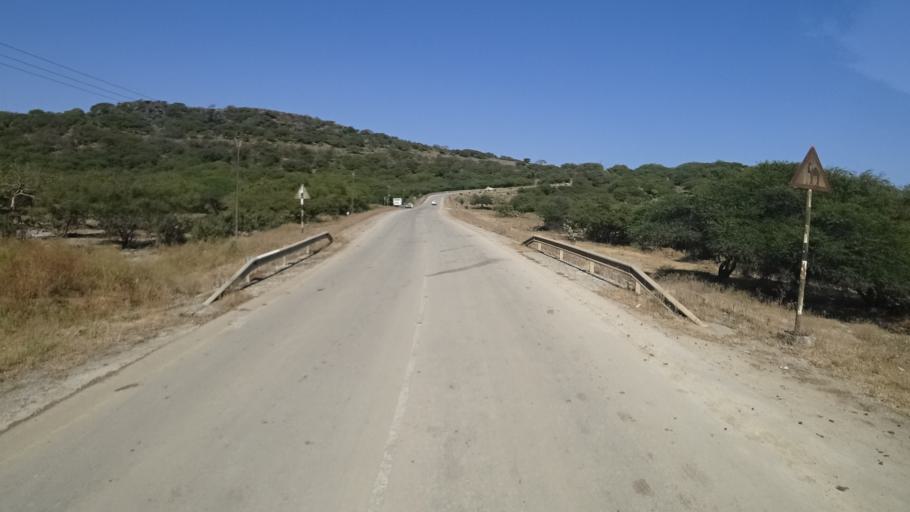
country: OM
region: Zufar
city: Salalah
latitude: 17.0690
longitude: 54.5995
